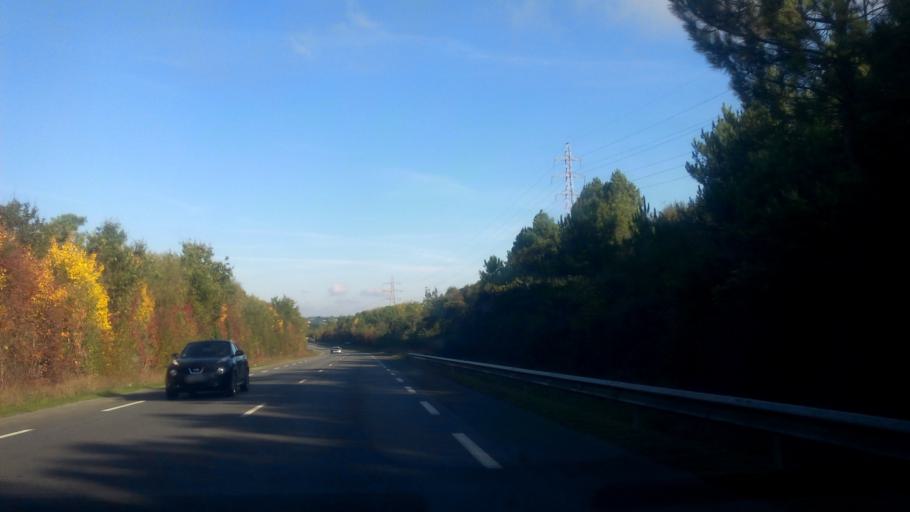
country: FR
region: Pays de la Loire
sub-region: Departement de la Loire-Atlantique
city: Saint-Nicolas-de-Redon
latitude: 47.6520
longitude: -2.0457
